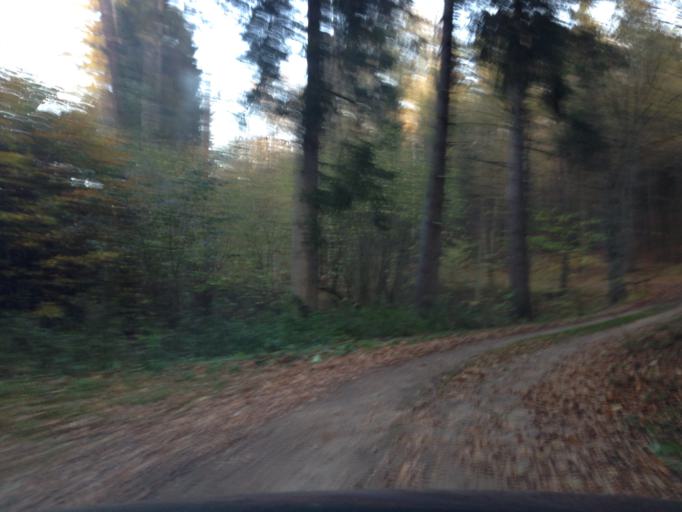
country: PL
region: Kujawsko-Pomorskie
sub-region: Powiat brodnicki
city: Gorzno
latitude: 53.2402
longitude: 19.7115
